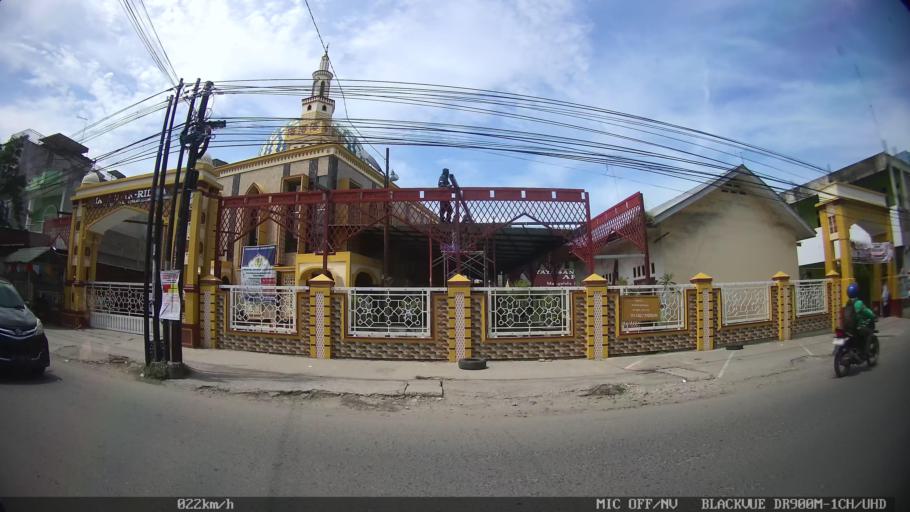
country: ID
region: North Sumatra
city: Labuhan Deli
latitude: 3.6885
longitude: 98.6629
